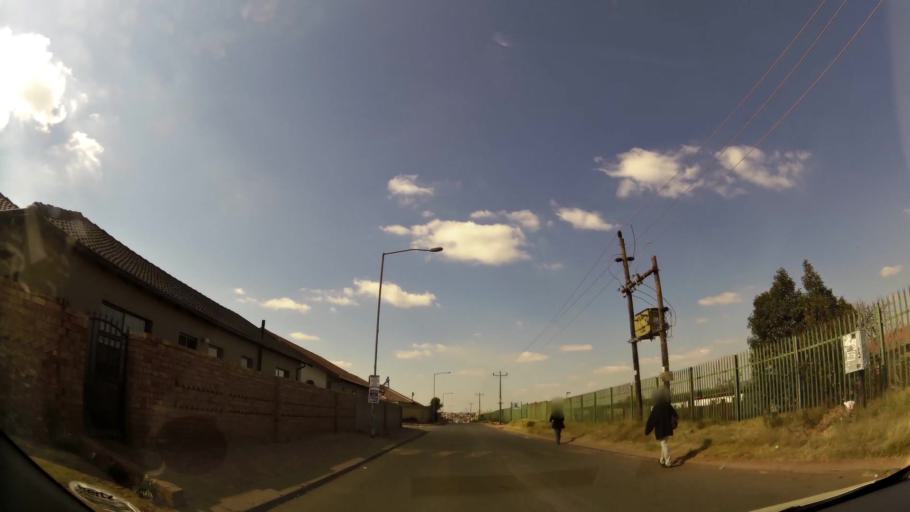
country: ZA
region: Gauteng
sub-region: West Rand District Municipality
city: Krugersdorp
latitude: -26.1645
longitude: 27.7845
